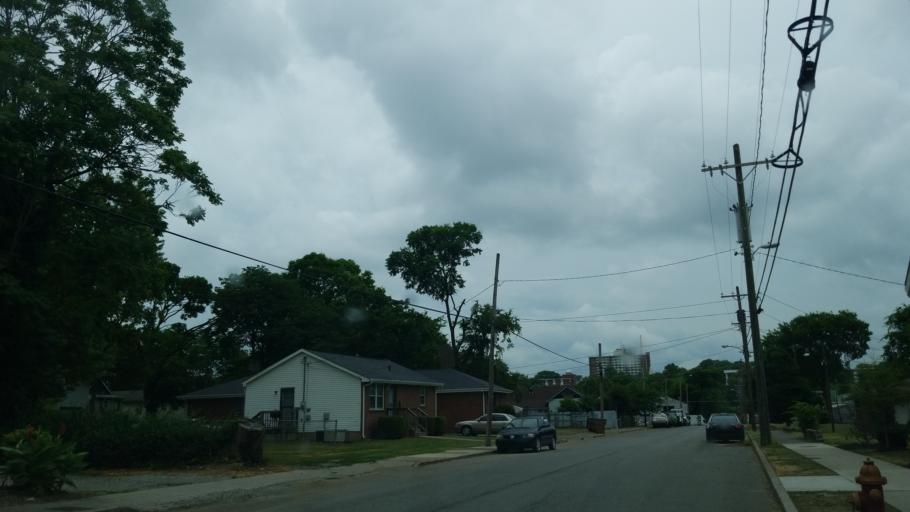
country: US
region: Tennessee
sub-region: Davidson County
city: Nashville
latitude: 36.1423
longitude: -86.7608
